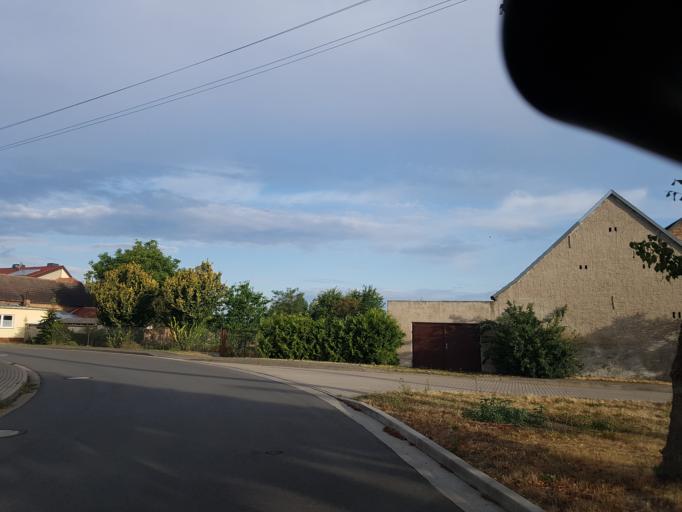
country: DE
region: Saxony-Anhalt
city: Holzdorf
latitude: 51.8045
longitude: 13.0833
